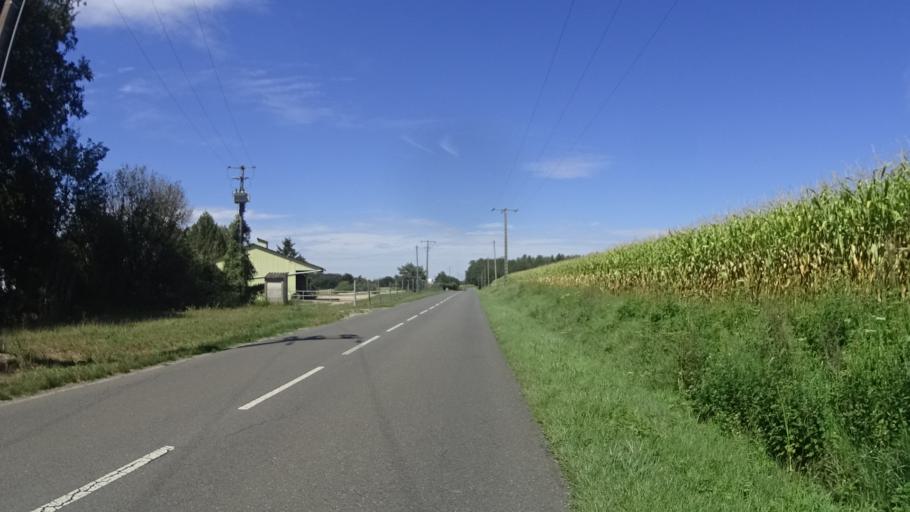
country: FR
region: Centre
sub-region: Departement du Loiret
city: Briare
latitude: 47.6148
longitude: 2.7561
